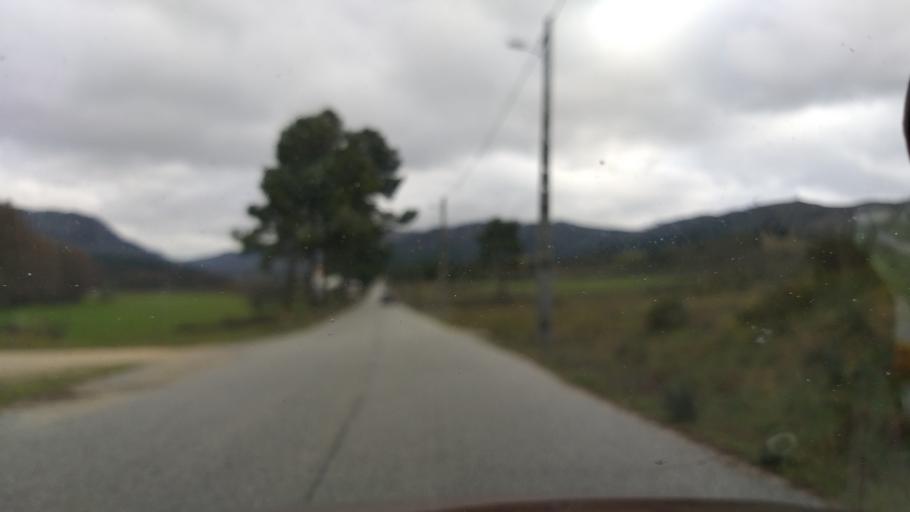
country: PT
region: Guarda
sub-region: Celorico da Beira
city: Celorico da Beira
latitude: 40.7010
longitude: -7.4458
